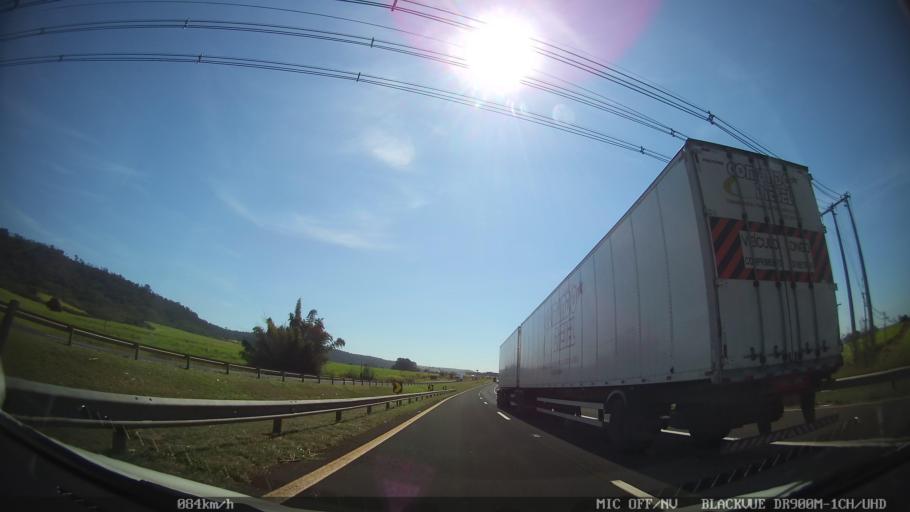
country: BR
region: Sao Paulo
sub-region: Sao Simao
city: Sao Simao
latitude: -21.5244
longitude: -47.6431
